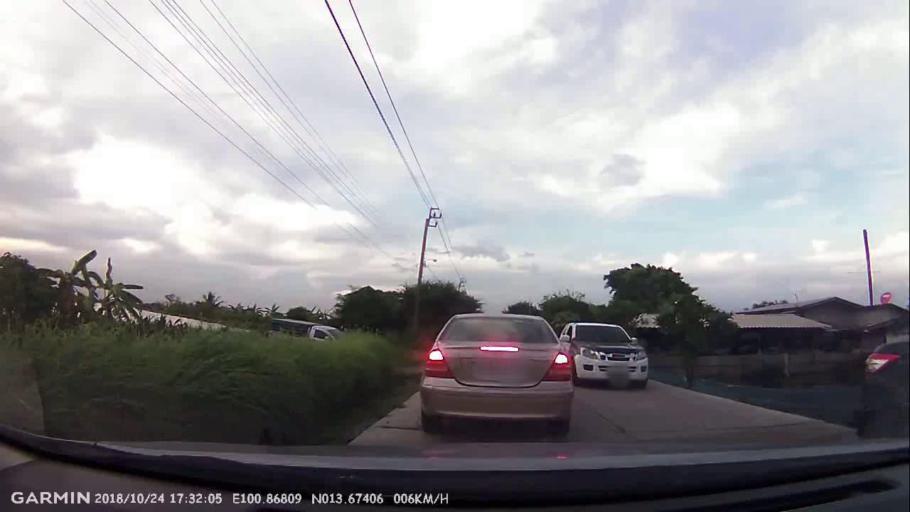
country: TH
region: Samut Prakan
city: Ban Khlong Bang Sao Thong
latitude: 13.6739
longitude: 100.8681
